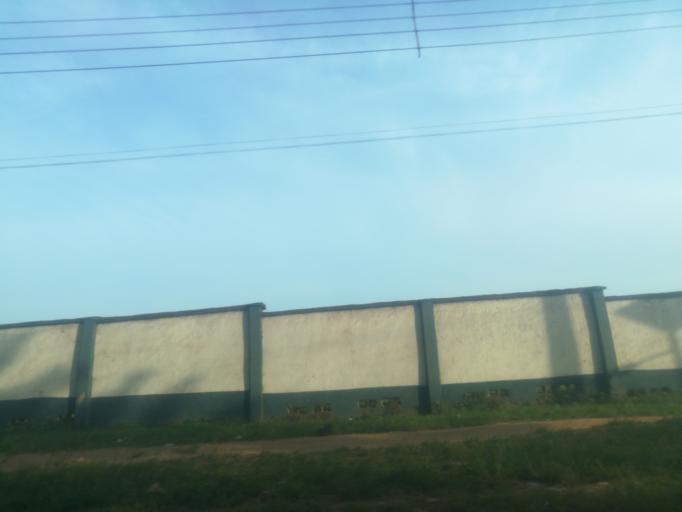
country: NG
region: Ogun
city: Abeokuta
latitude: 7.1272
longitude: 3.3254
